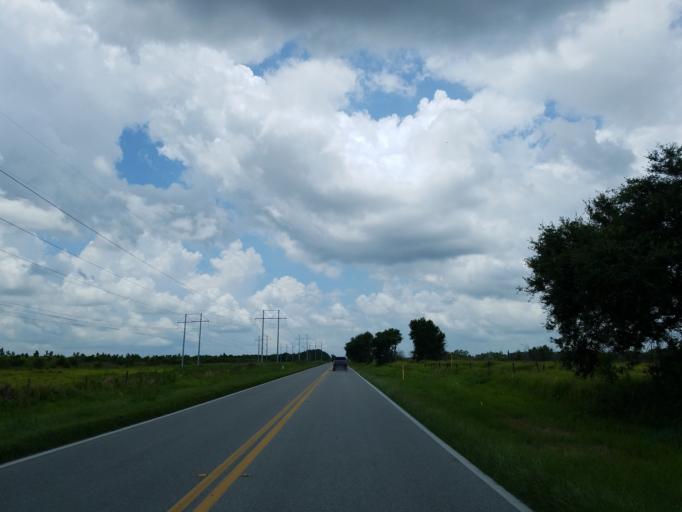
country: US
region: Florida
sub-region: Polk County
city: Willow Oak
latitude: 27.8507
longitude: -82.0309
